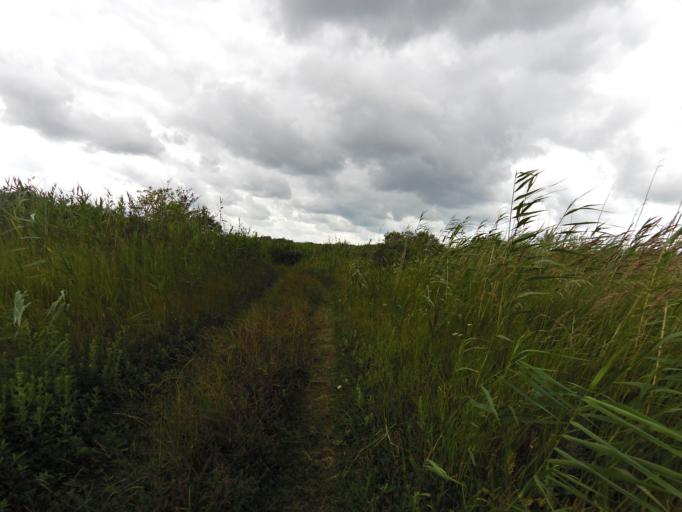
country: NL
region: South Holland
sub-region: Gemeente Goeree-Overflakkee
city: Goedereede
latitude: 51.8400
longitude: 3.9895
